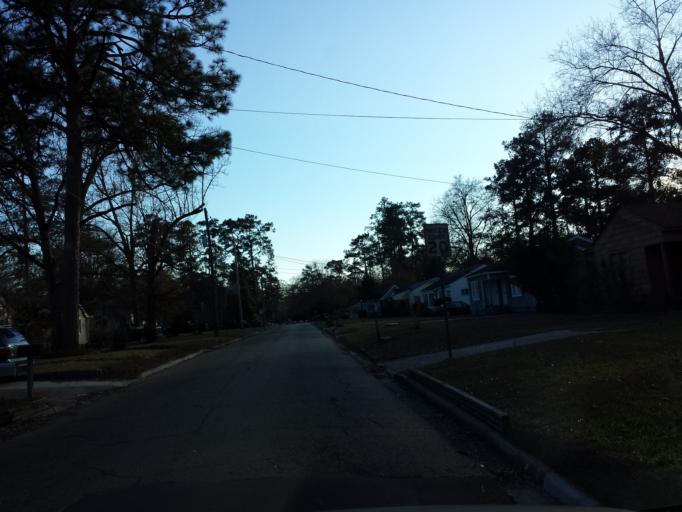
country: US
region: Mississippi
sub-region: Forrest County
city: Hattiesburg
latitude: 31.3209
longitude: -89.3131
